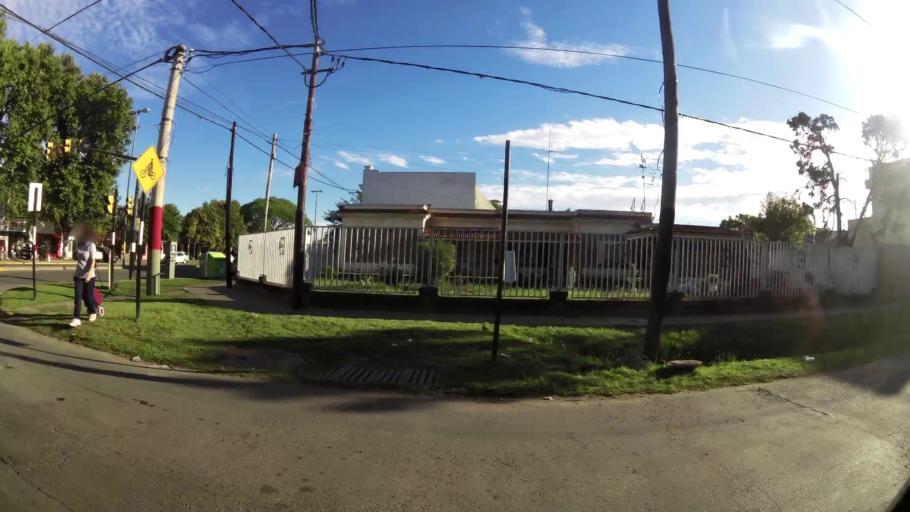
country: AR
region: Santa Fe
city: Gobernador Galvez
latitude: -32.9887
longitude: -60.6730
